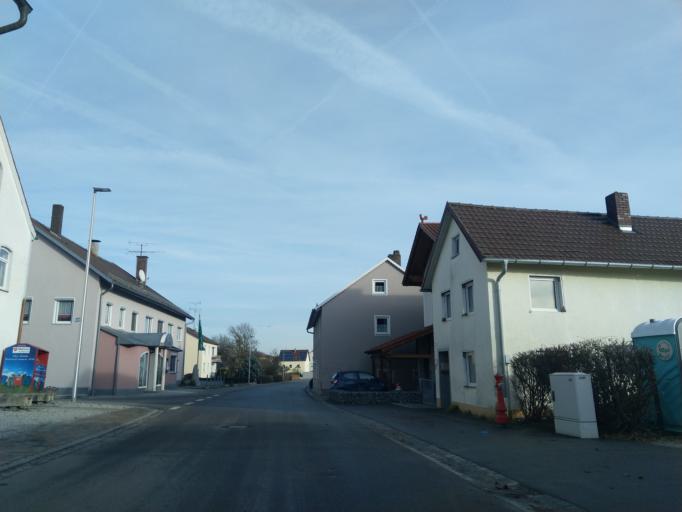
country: DE
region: Bavaria
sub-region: Lower Bavaria
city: Otzing
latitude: 48.7594
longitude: 12.8040
